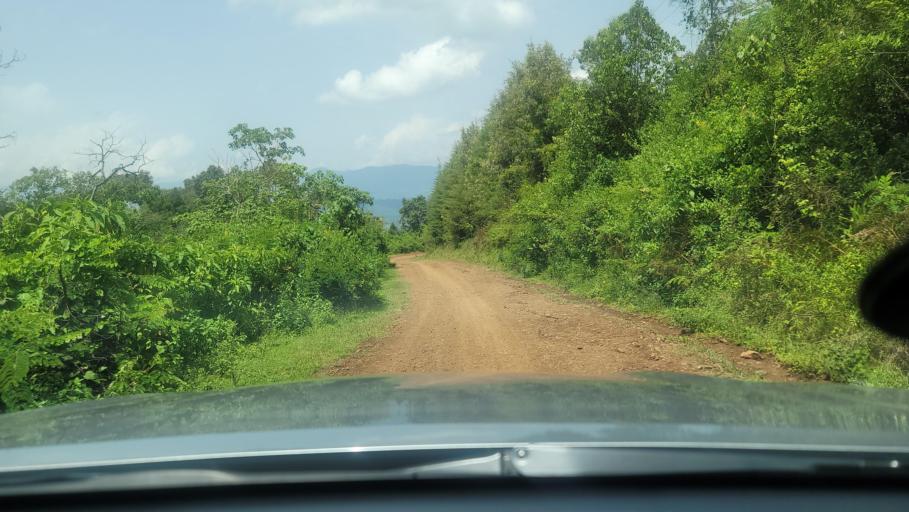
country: ET
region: Oromiya
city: Agaro
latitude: 7.8138
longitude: 36.4125
